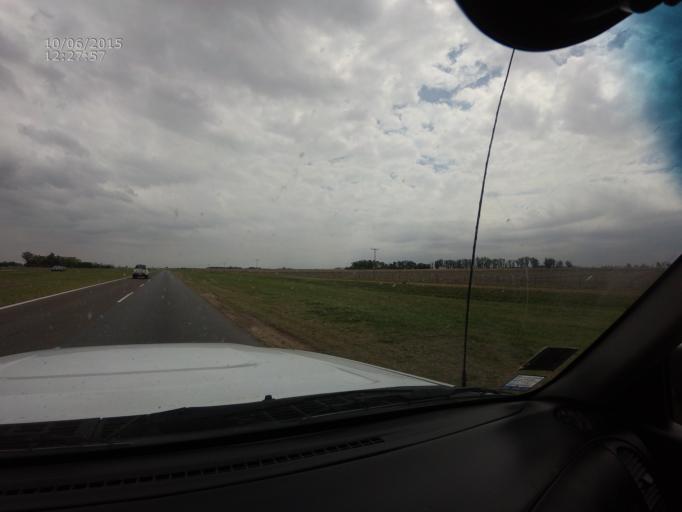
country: AR
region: Santa Fe
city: Carcarana
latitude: -32.8977
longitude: -61.0500
